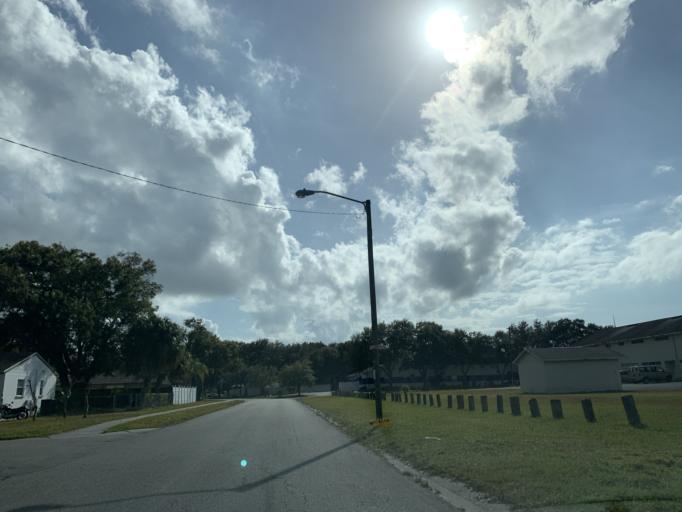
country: US
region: Florida
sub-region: Hillsborough County
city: Tampa
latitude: 27.9060
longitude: -82.5172
